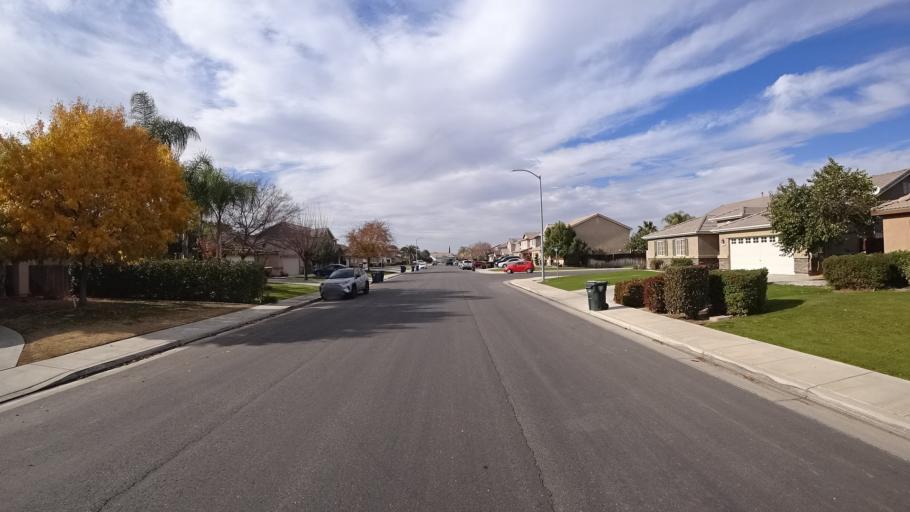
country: US
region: California
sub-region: Kern County
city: Rosedale
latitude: 35.4219
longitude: -119.1379
